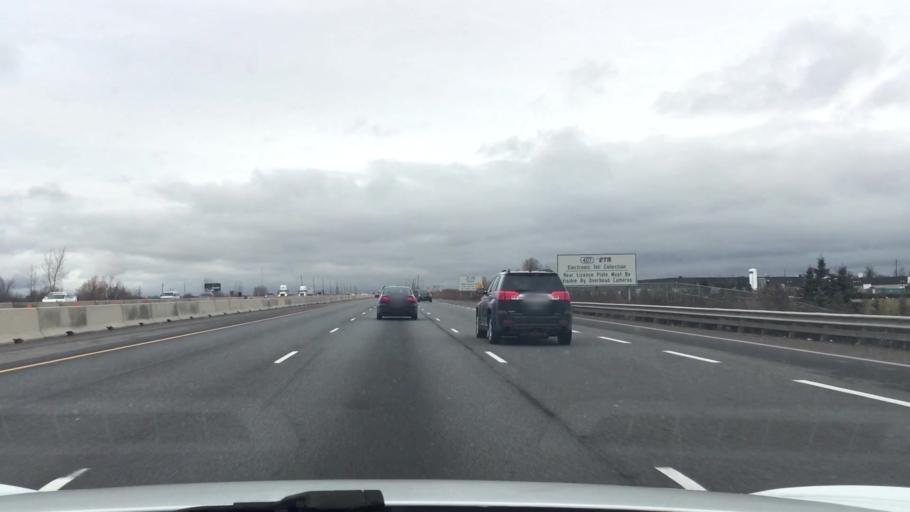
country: CA
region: Ontario
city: Etobicoke
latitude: 43.7377
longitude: -79.6278
